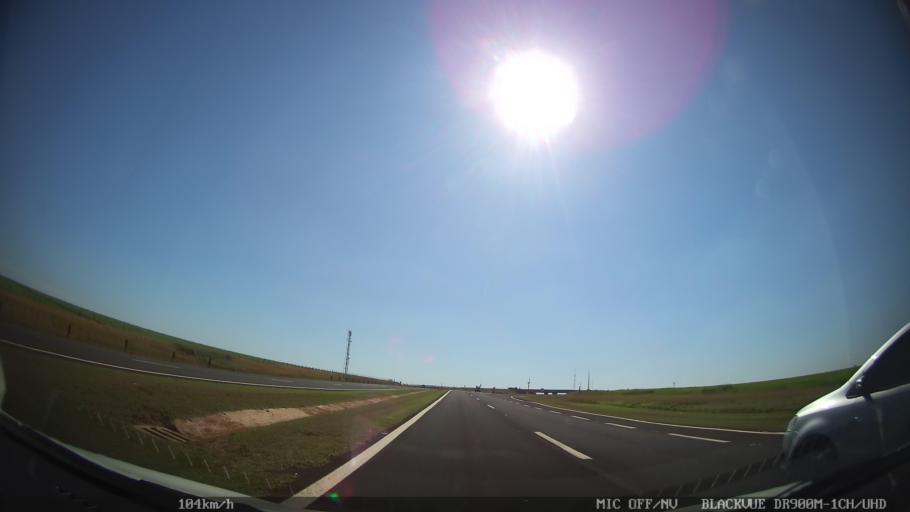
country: BR
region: Sao Paulo
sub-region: Ribeirao Preto
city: Ribeirao Preto
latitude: -21.1702
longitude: -47.8986
